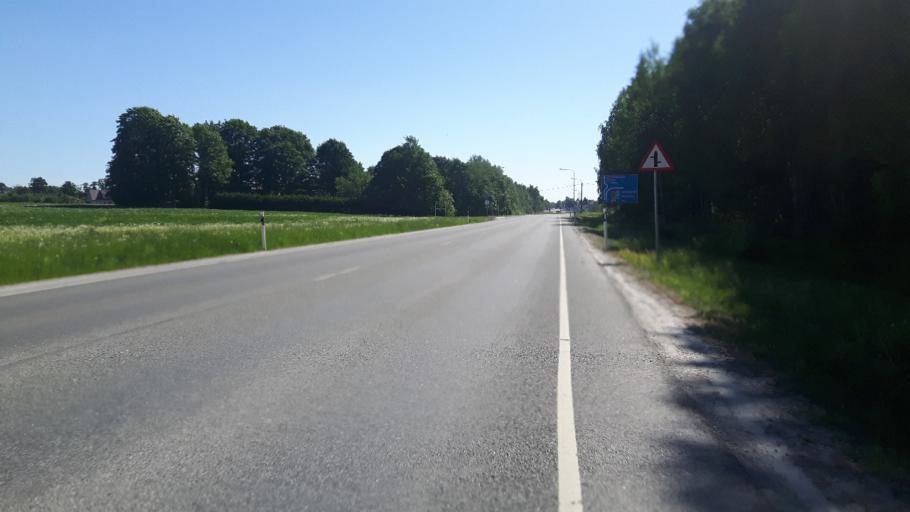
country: EE
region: Raplamaa
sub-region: Rapla vald
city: Rapla
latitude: 59.0174
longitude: 24.8049
